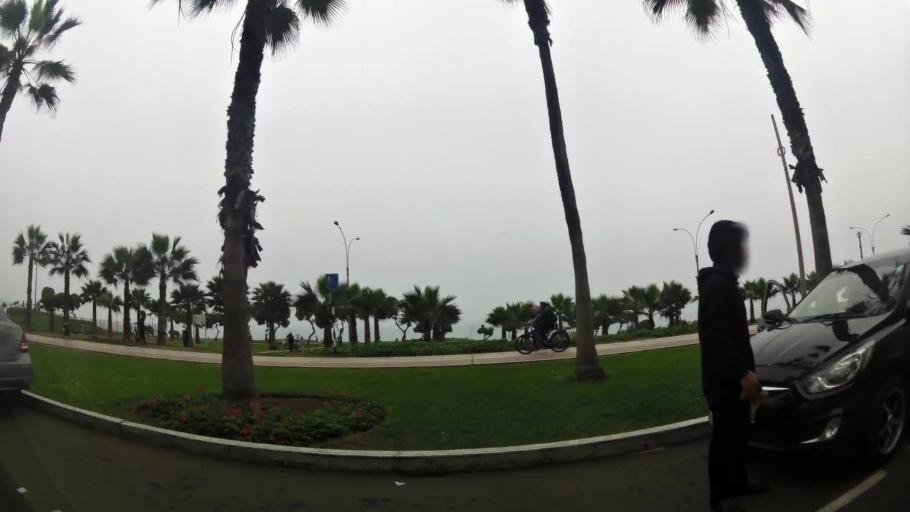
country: PE
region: Lima
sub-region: Lima
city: San Isidro
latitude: -12.1168
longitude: -77.0470
